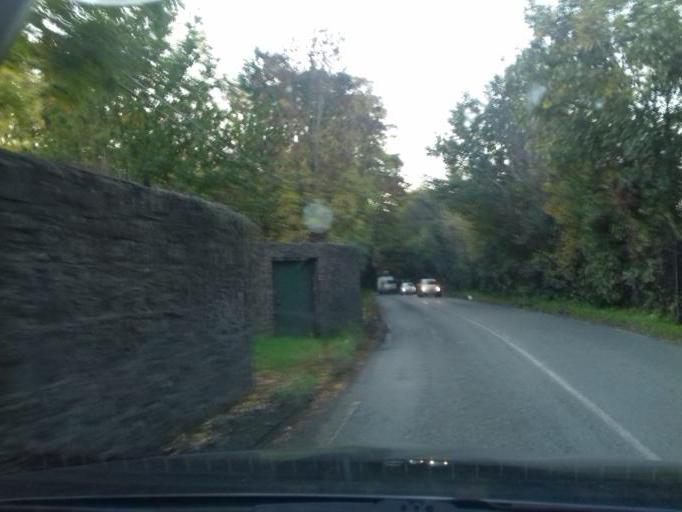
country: IE
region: Leinster
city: Hartstown
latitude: 53.3798
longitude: -6.4252
